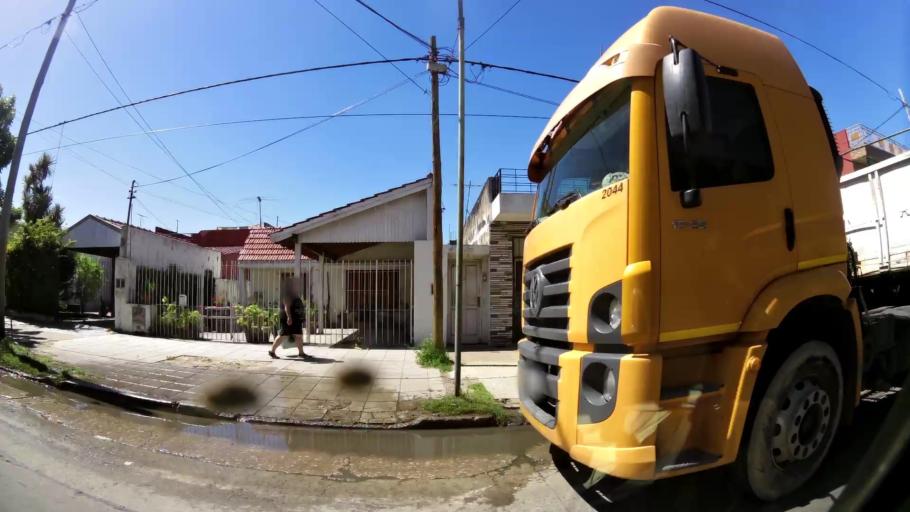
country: AR
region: Buenos Aires
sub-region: Partido de Quilmes
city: Quilmes
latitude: -34.7201
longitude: -58.3093
